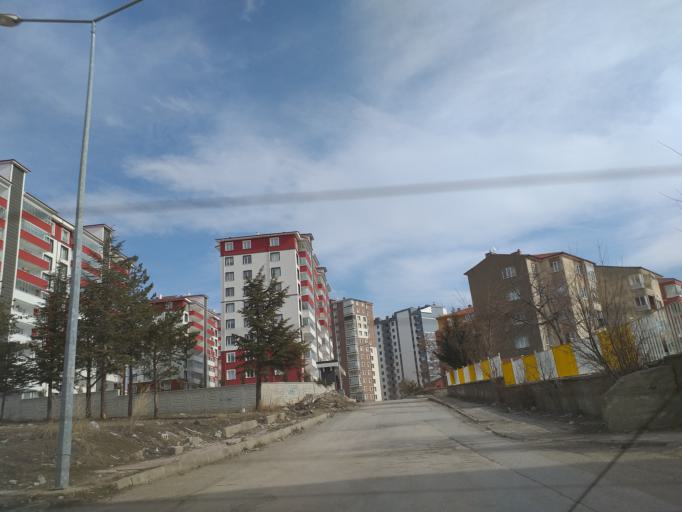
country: TR
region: Yozgat
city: Yozgat
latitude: 39.8310
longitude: 34.8208
